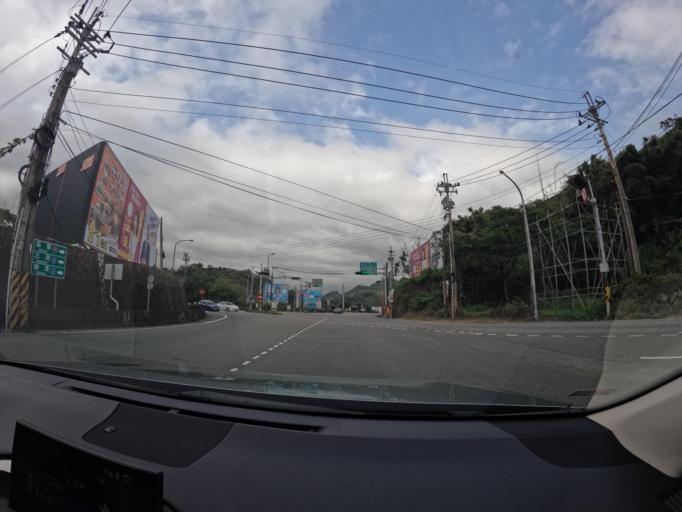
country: TW
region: Taiwan
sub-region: Miaoli
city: Miaoli
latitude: 24.4554
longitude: 120.8775
